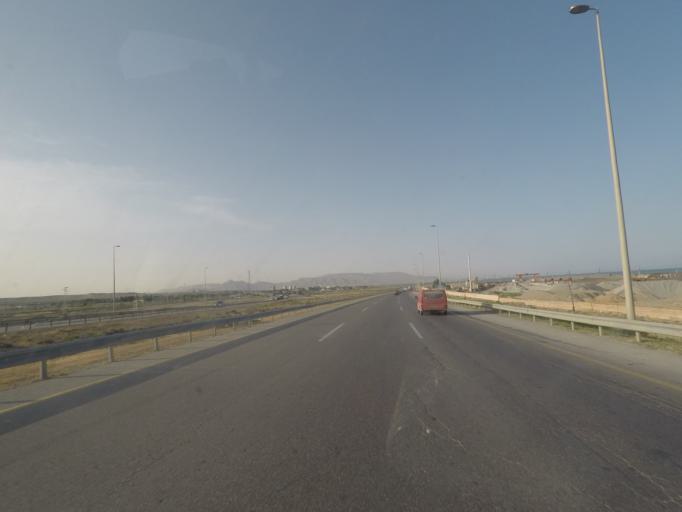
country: AZ
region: Baki
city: Qobustan
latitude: 40.1547
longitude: 49.4587
